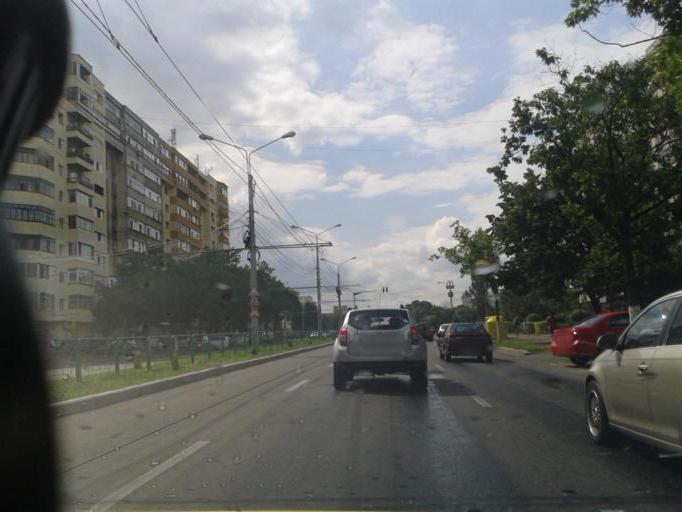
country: RO
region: Prahova
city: Ploiesti
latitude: 44.9511
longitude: 26.0016
